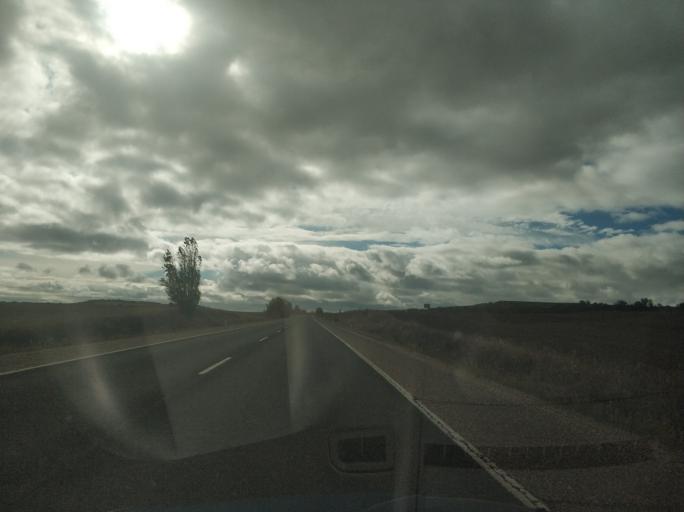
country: ES
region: Castille and Leon
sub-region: Provincia de Zamora
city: Castrillo de la Guarena
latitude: 41.2159
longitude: -5.3190
